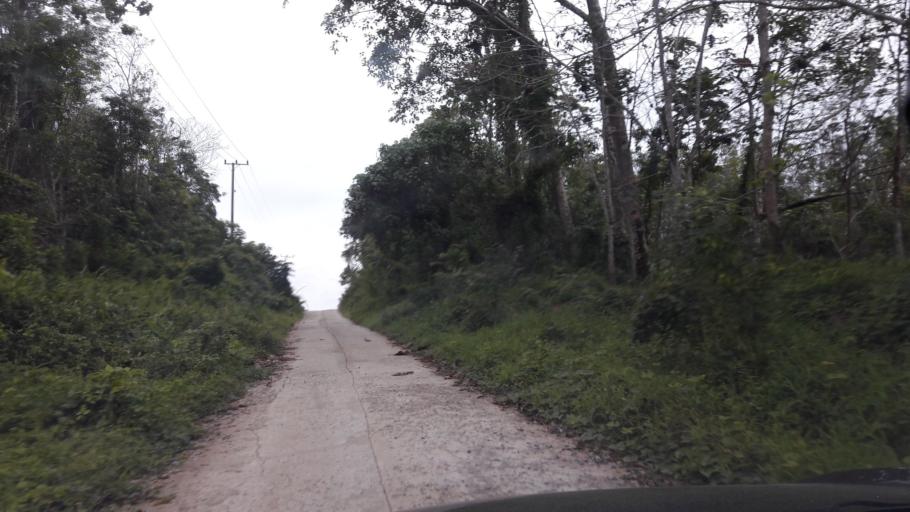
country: ID
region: South Sumatra
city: Gunungmenang
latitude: -3.1971
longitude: 103.8087
